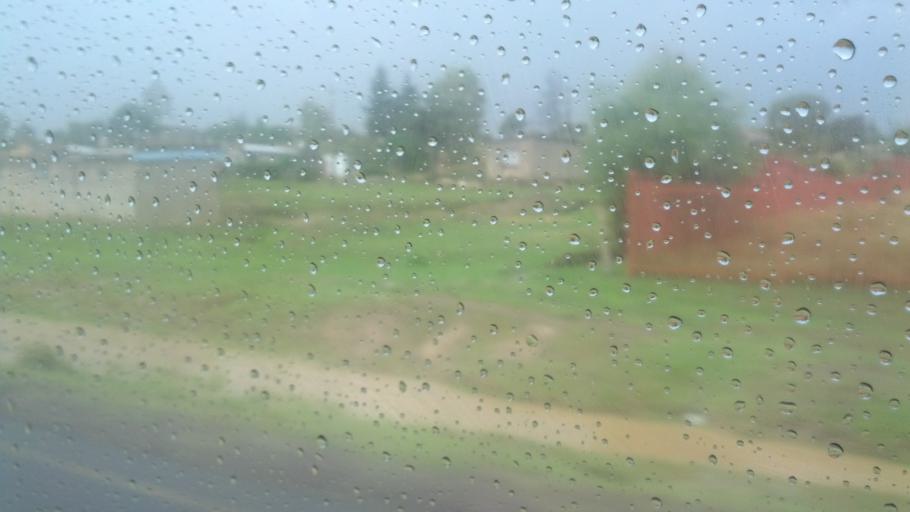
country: LS
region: Mafeteng
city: Mafeteng
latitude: -29.8036
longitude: 27.2149
